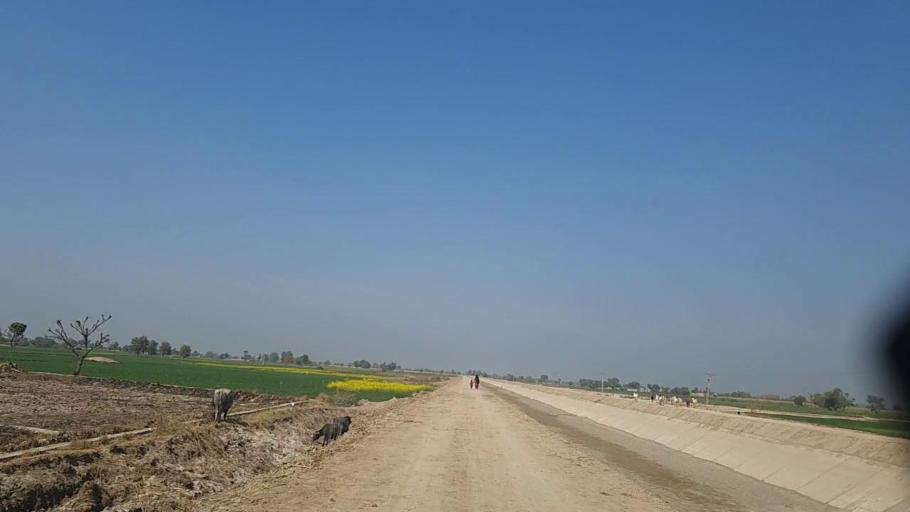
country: PK
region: Sindh
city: Sakrand
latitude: 26.1540
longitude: 68.3296
